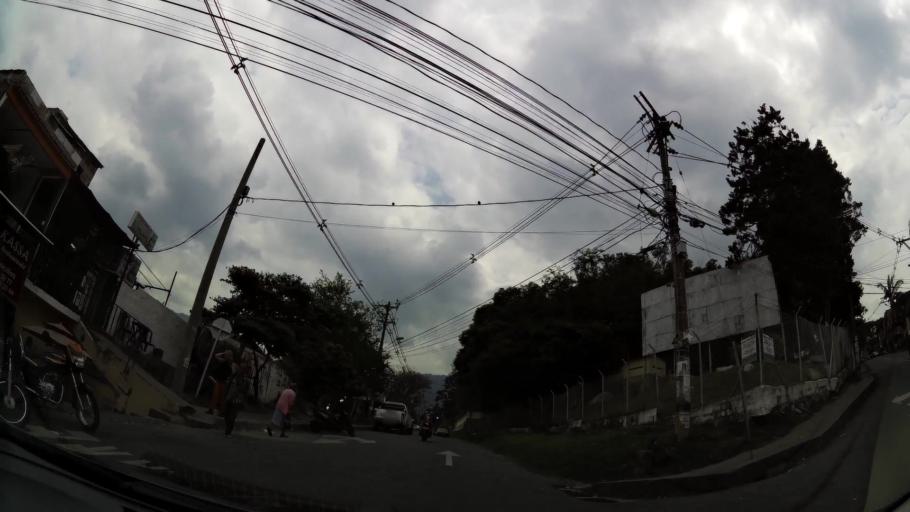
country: CO
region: Antioquia
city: Medellin
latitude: 6.2348
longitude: -75.5488
